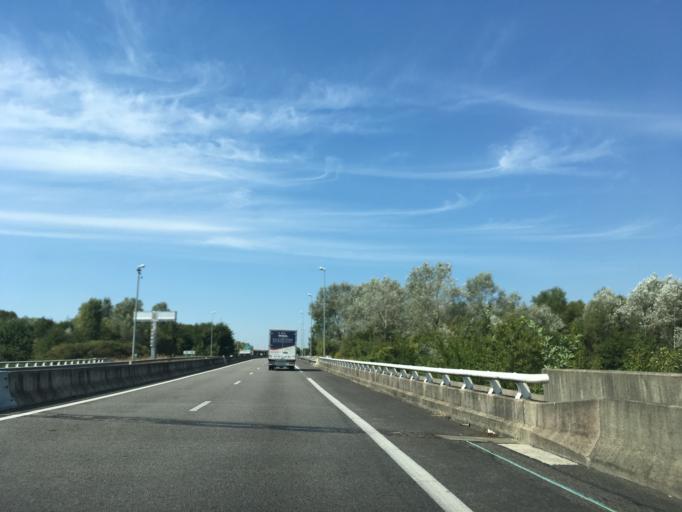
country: FR
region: Ile-de-France
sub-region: Departement des Yvelines
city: Villennes-sur-Seine
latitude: 48.9199
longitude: 2.0084
